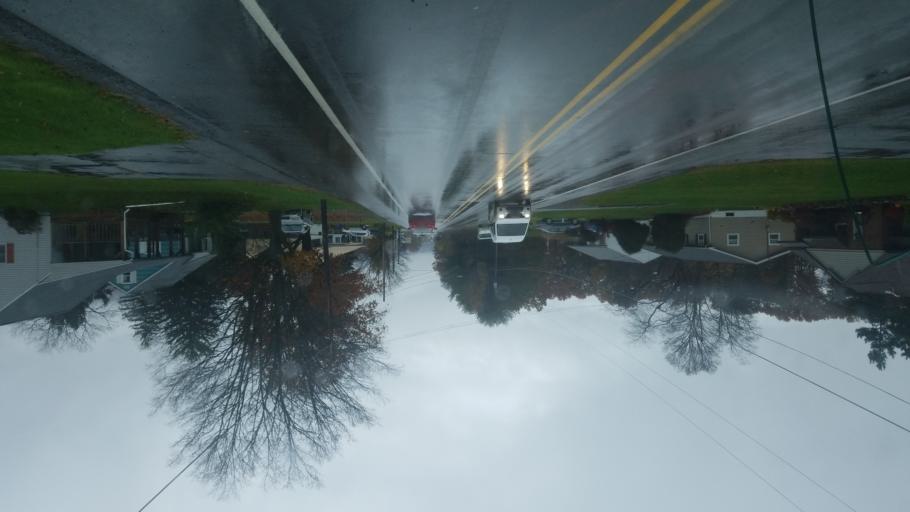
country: US
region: Pennsylvania
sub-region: Clinton County
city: Mill Hall
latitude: 41.1124
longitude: -77.4959
